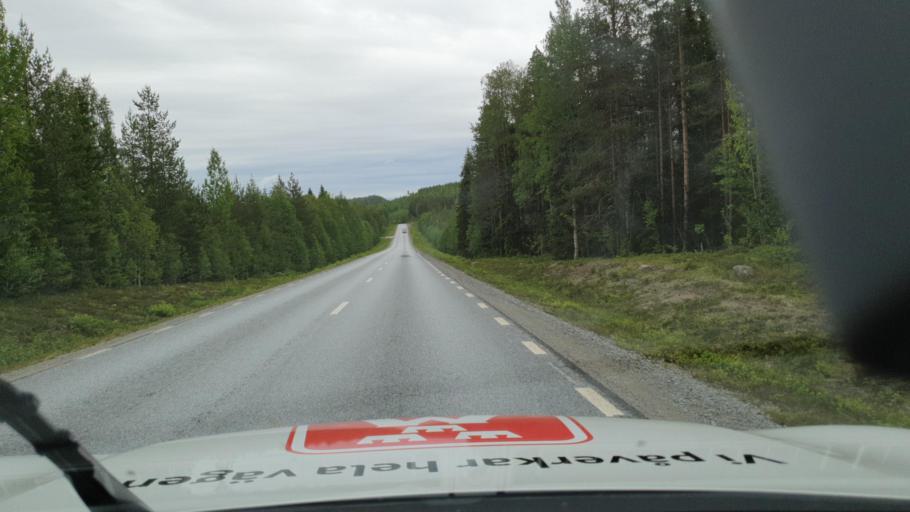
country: SE
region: Vaesterbotten
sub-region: Lycksele Kommun
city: Lycksele
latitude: 64.0449
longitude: 18.5745
